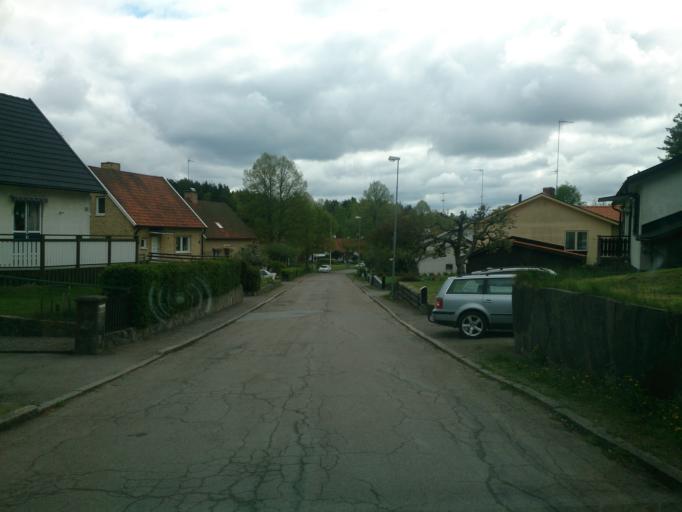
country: SE
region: OEstergoetland
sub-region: Atvidabergs Kommun
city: Atvidaberg
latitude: 58.2119
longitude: 16.0082
